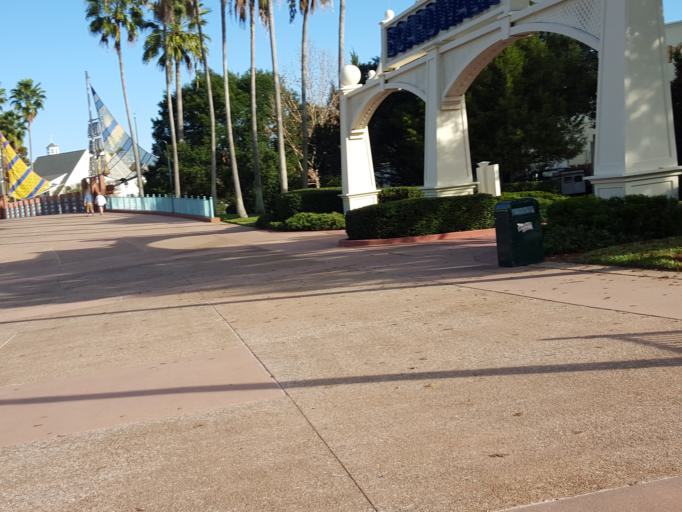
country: US
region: Florida
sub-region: Osceola County
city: Celebration
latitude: 28.3672
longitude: -81.5586
